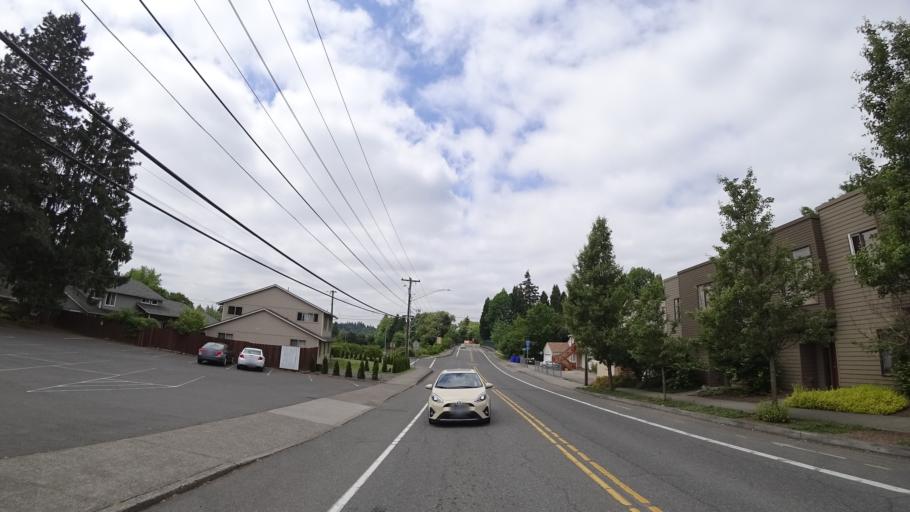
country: US
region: Oregon
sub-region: Clackamas County
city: Lake Oswego
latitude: 45.4635
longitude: -122.6975
